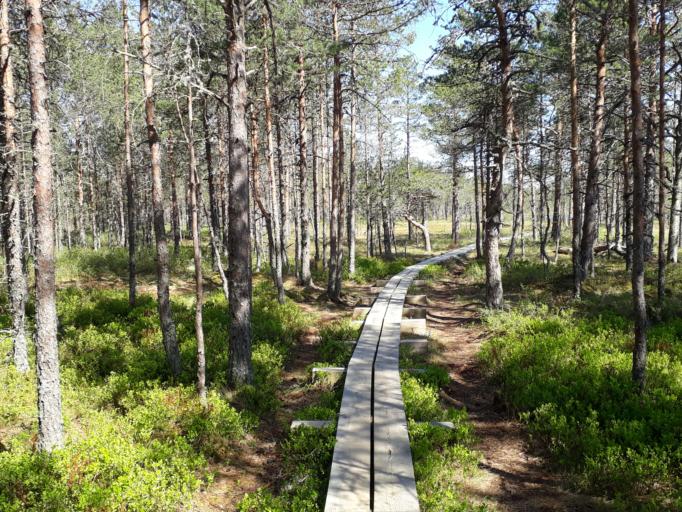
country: EE
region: Harju
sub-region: Loksa linn
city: Loksa
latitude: 59.4719
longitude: 25.6629
